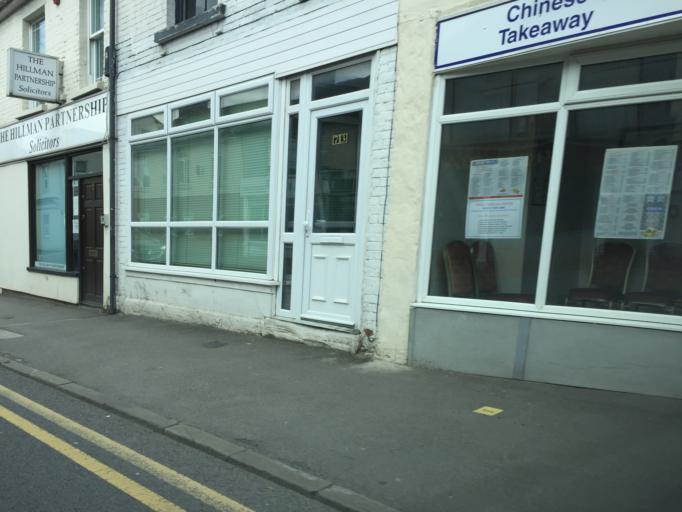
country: GB
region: England
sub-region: Borough of Swindon
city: Swindon
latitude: 51.5546
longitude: -1.7773
